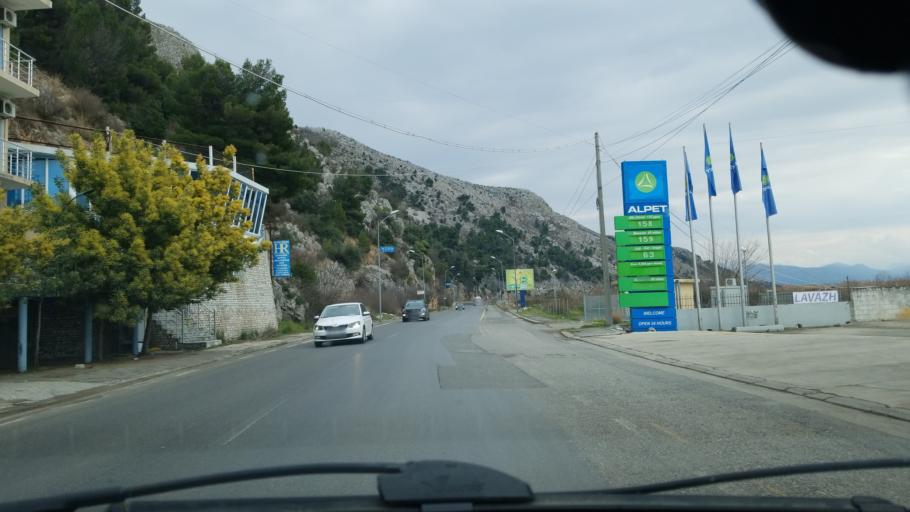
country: AL
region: Lezhe
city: Shengjin
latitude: 41.8065
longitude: 19.6088
